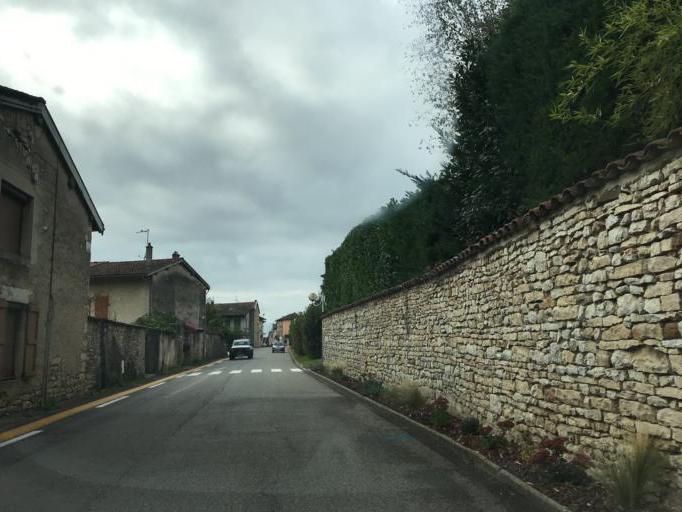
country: FR
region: Rhone-Alpes
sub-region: Departement de l'Ain
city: Jasseron
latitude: 46.2124
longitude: 5.3278
